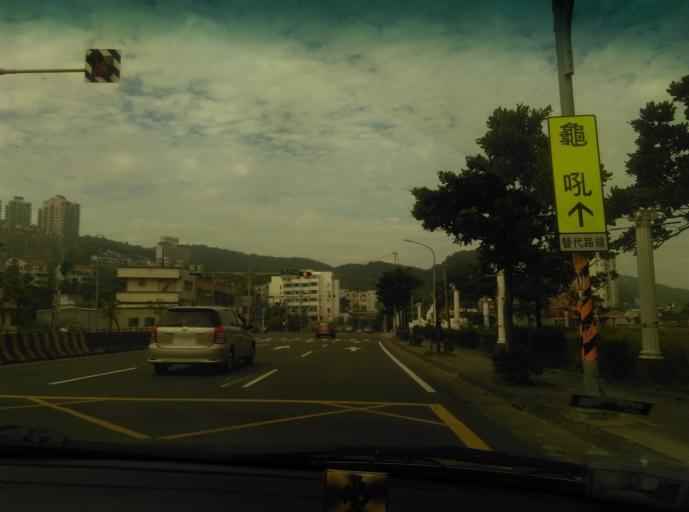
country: TW
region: Taiwan
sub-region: Keelung
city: Keelung
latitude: 25.1886
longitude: 121.6833
